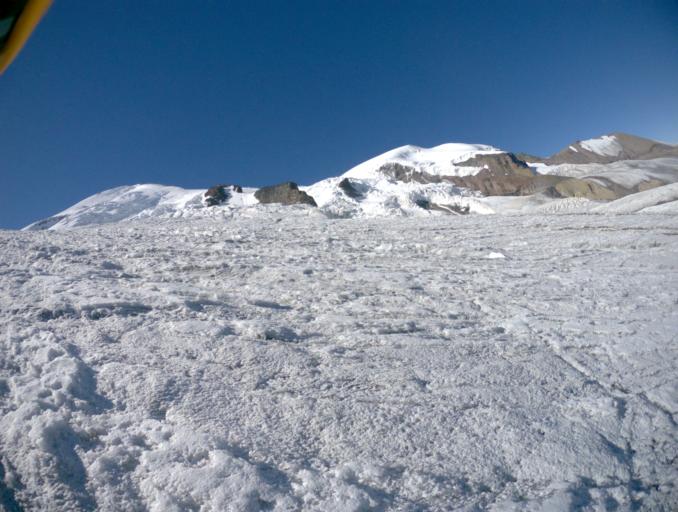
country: RU
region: Kabardino-Balkariya
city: Terskol
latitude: 43.3872
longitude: 42.4355
